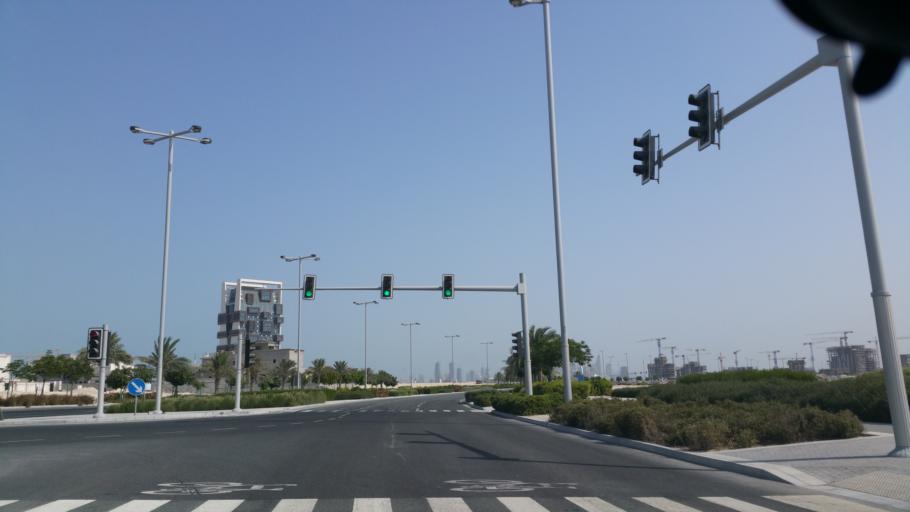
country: QA
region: Baladiyat Umm Salal
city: Umm Salal Muhammad
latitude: 25.4377
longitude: 51.5144
